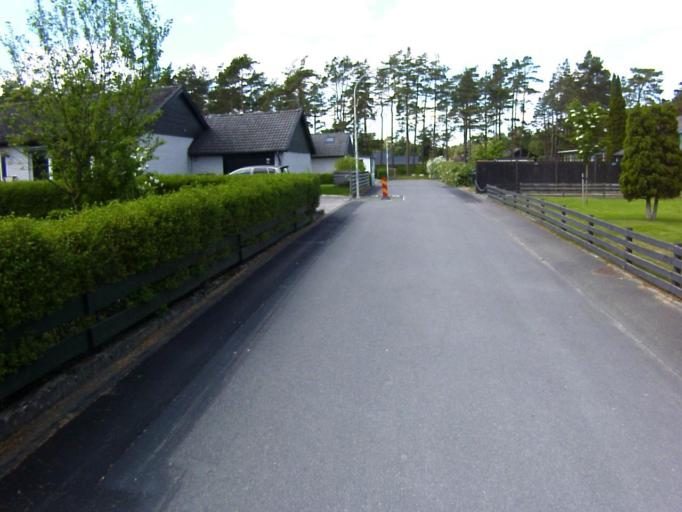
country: SE
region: Skane
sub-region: Kristianstads Kommun
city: Ahus
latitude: 55.9460
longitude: 14.2780
